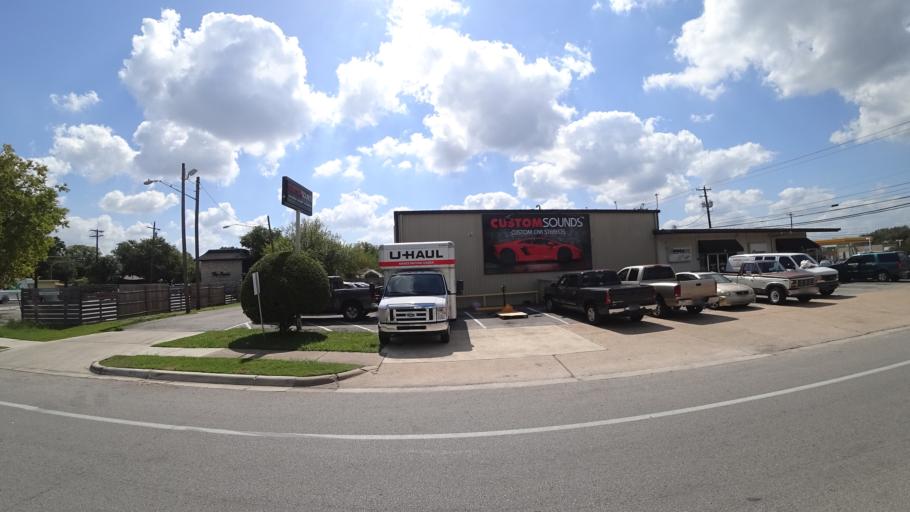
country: US
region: Texas
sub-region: Williamson County
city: Jollyville
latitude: 30.3628
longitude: -97.7285
